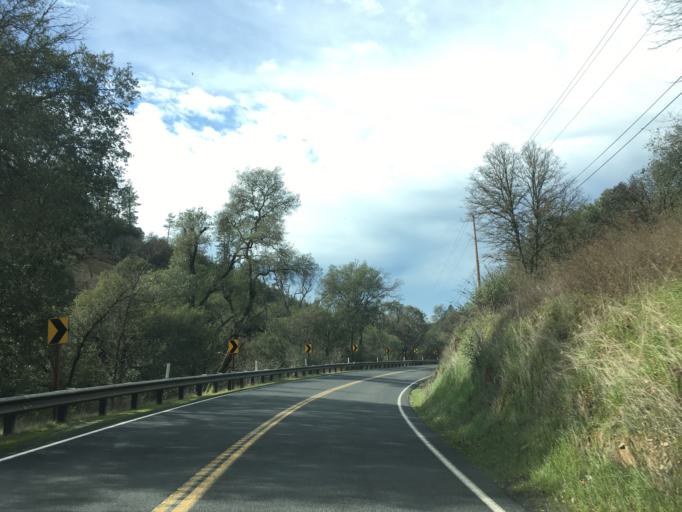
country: US
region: California
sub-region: Calaveras County
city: San Andreas
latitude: 38.1905
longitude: -120.6057
